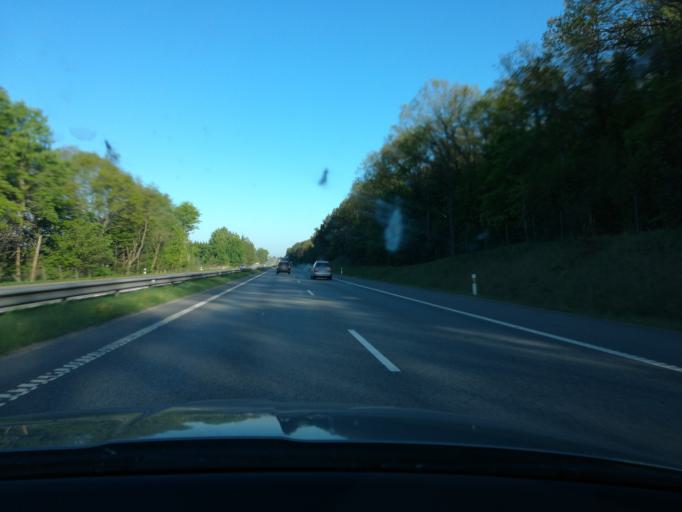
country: LT
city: Ziezmariai
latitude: 54.8055
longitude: 24.4909
